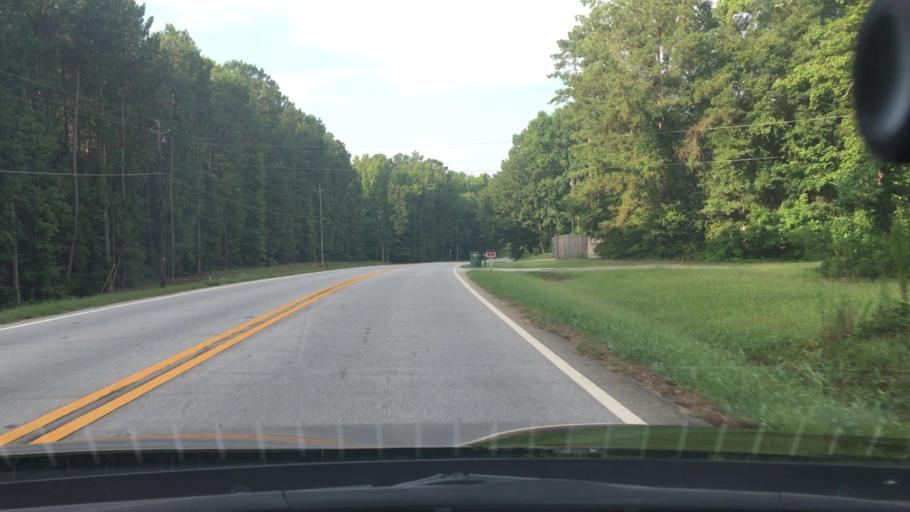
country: US
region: Georgia
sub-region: Fayette County
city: Peachtree City
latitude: 33.3554
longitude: -84.6365
